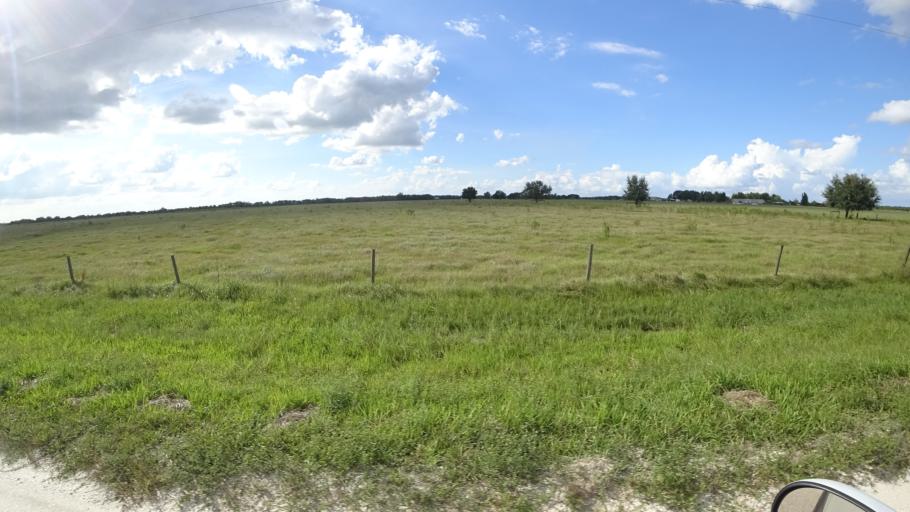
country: US
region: Florida
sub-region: Sarasota County
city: Lake Sarasota
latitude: 27.3365
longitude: -82.1780
